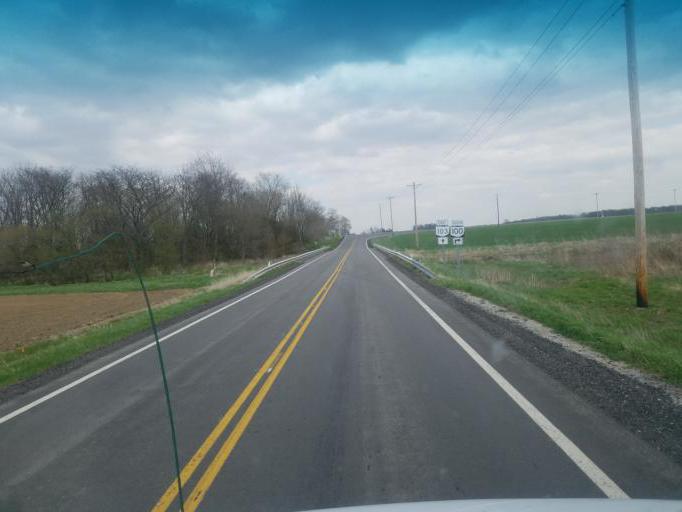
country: US
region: Ohio
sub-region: Crawford County
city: Bucyrus
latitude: 40.9504
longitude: -83.0682
